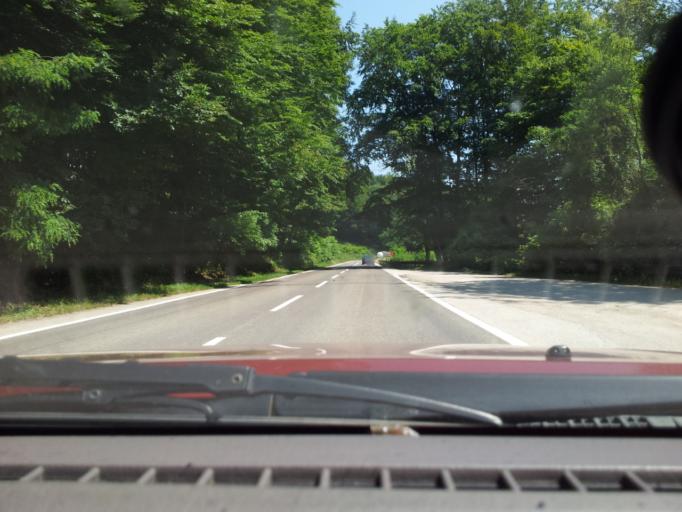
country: SK
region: Trnavsky
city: Smolenice
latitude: 48.5623
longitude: 17.4587
